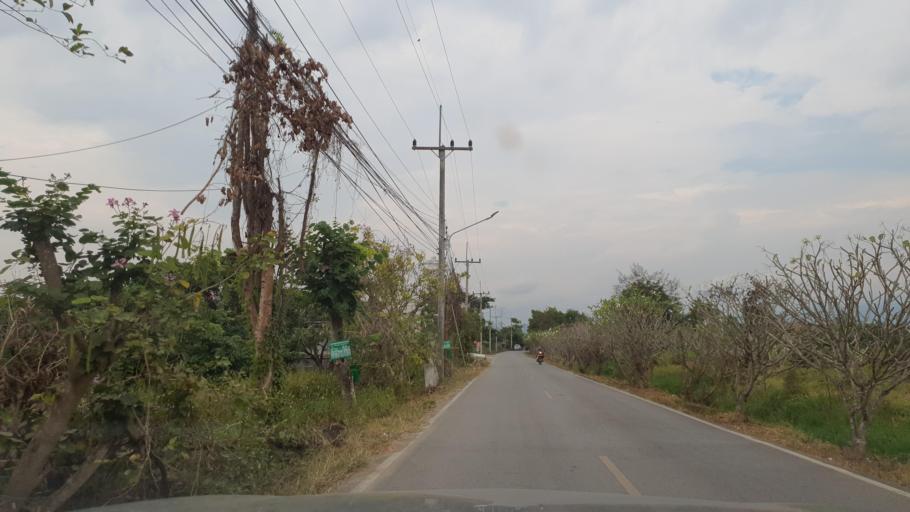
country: TH
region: Chiang Mai
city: Hang Dong
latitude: 18.6753
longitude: 98.9449
